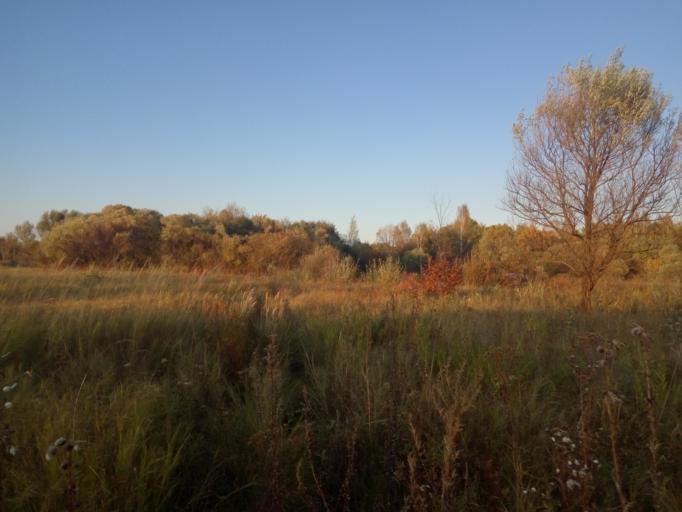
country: RU
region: Khabarovsk Krai
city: Khor
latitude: 47.7026
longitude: 134.9641
